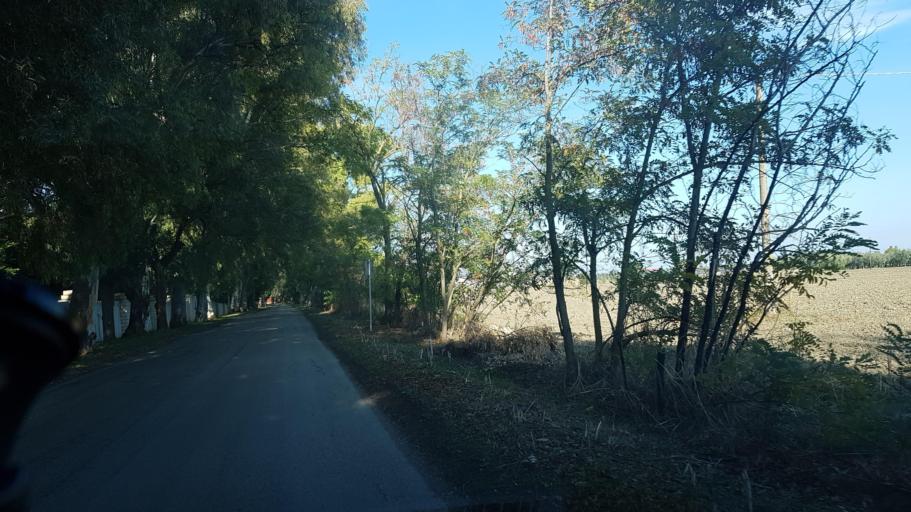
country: IT
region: Apulia
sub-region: Provincia di Foggia
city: Carapelle
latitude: 41.3933
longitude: 15.6516
